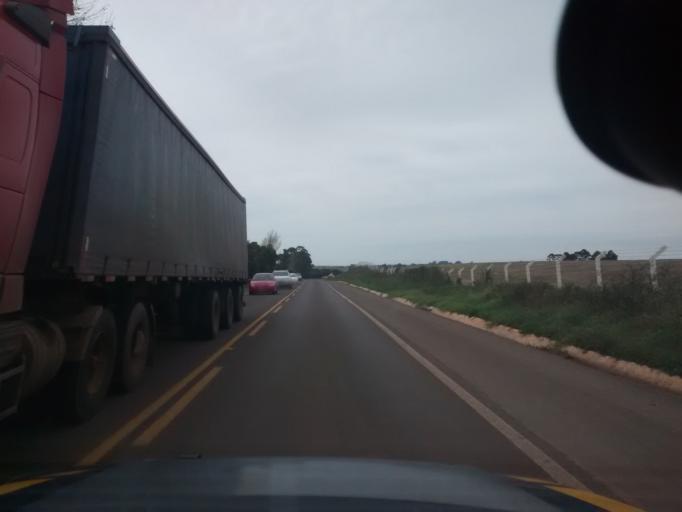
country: BR
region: Rio Grande do Sul
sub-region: Vacaria
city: Vacaria
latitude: -28.4364
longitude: -51.0058
